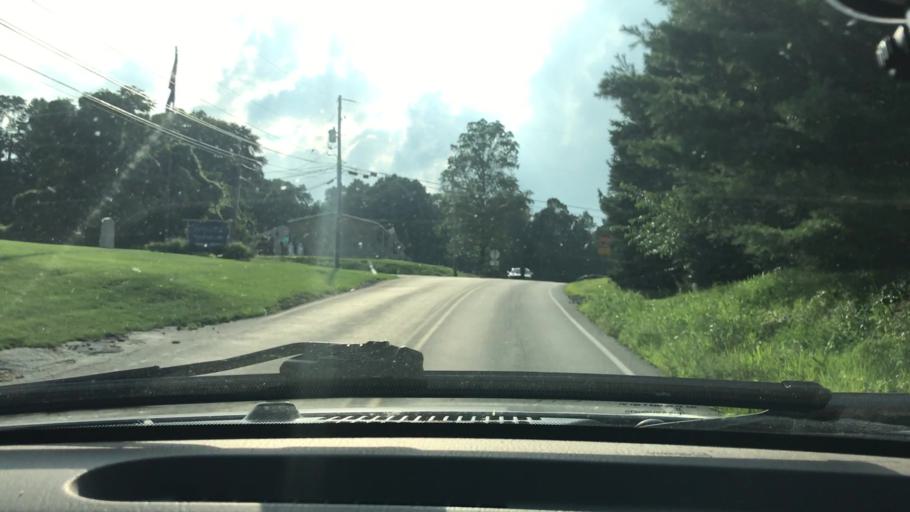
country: US
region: Pennsylvania
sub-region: Lebanon County
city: Campbelltown
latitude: 40.2279
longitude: -76.6242
